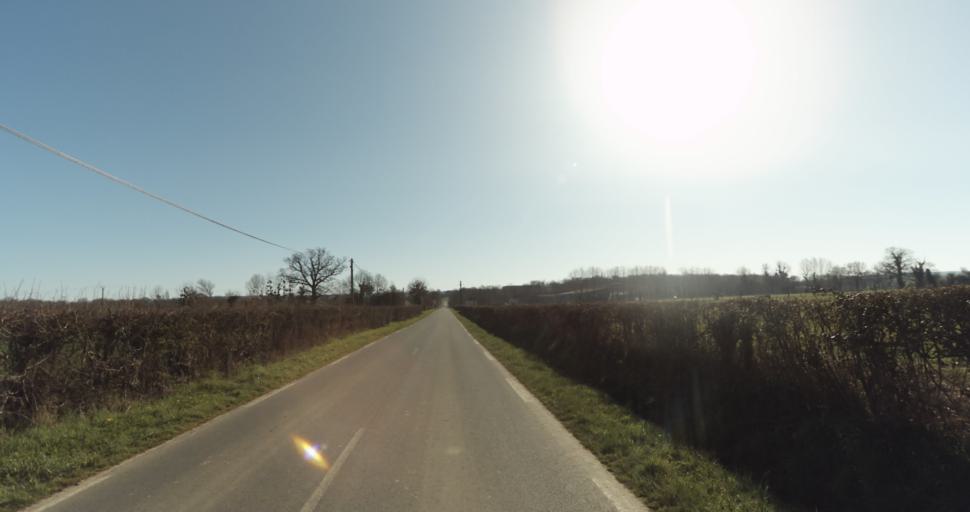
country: FR
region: Lower Normandy
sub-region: Departement du Calvados
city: Saint-Pierre-sur-Dives
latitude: 48.9897
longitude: -0.0122
